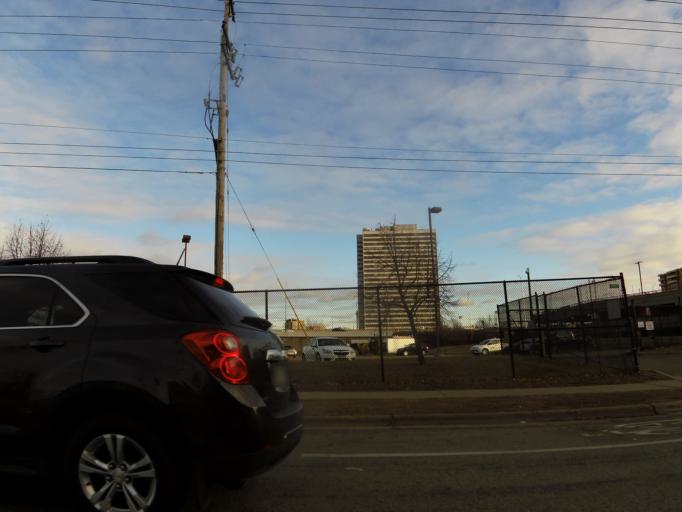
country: US
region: Minnesota
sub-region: Hennepin County
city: Minneapolis
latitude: 44.9774
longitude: -93.2479
